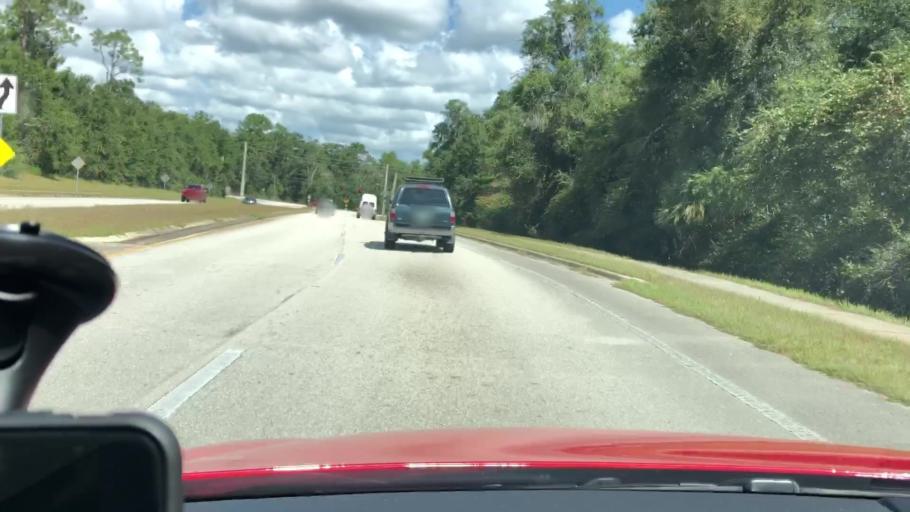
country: US
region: Florida
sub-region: Volusia County
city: Orange City
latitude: 28.9467
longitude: -81.2710
